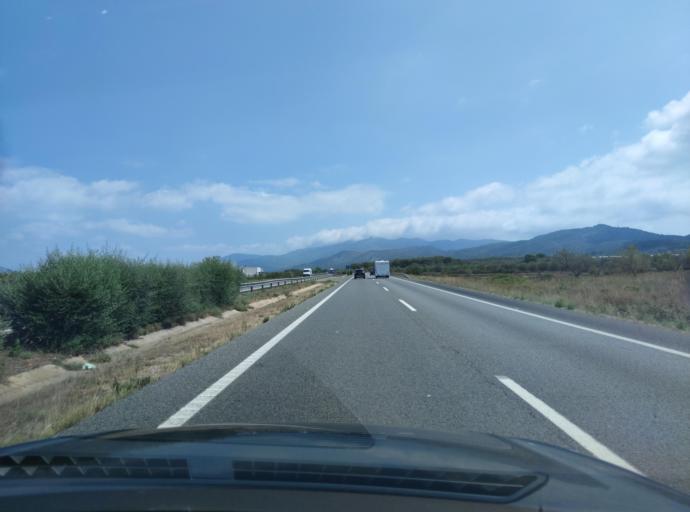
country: ES
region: Catalonia
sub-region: Provincia de Tarragona
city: Ulldecona
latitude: 40.5751
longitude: 0.4433
